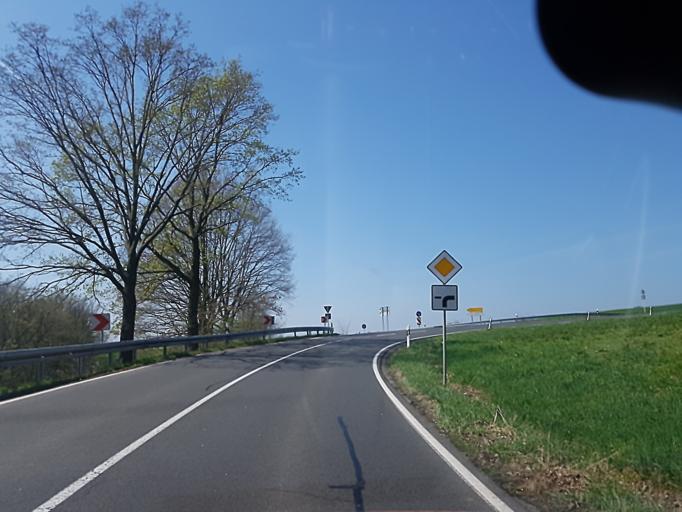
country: DE
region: Saxony
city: Leisnig
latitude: 51.1796
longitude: 12.9077
